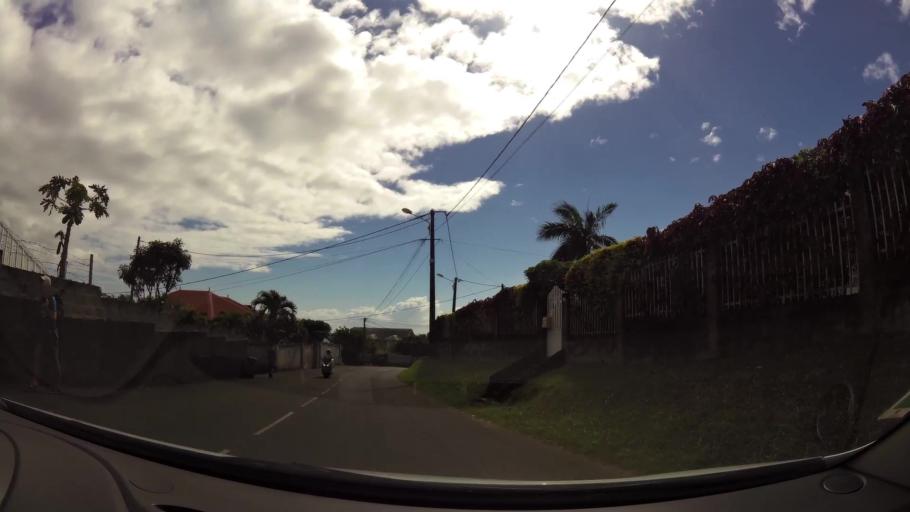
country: RE
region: Reunion
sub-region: Reunion
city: Saint-Denis
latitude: -20.9252
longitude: 55.4903
